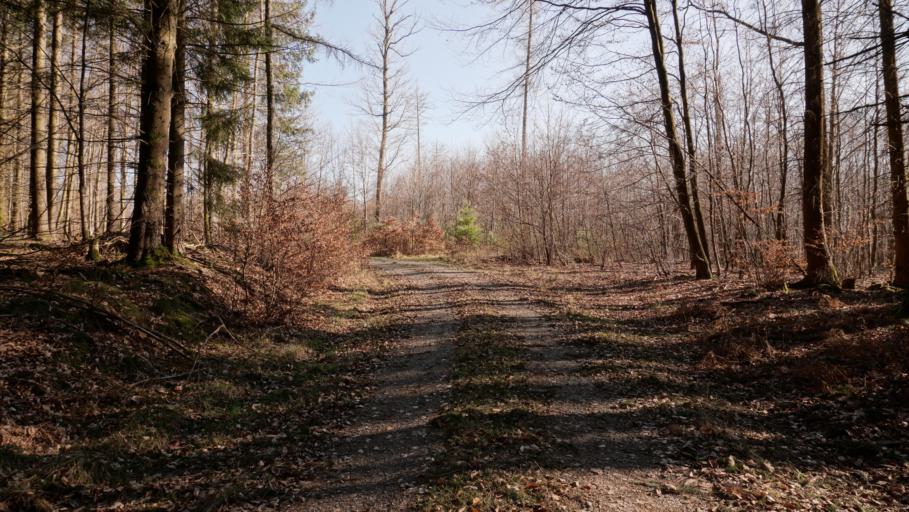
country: DE
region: Baden-Wuerttemberg
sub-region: Karlsruhe Region
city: Fahrenbach
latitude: 49.4441
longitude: 9.1374
